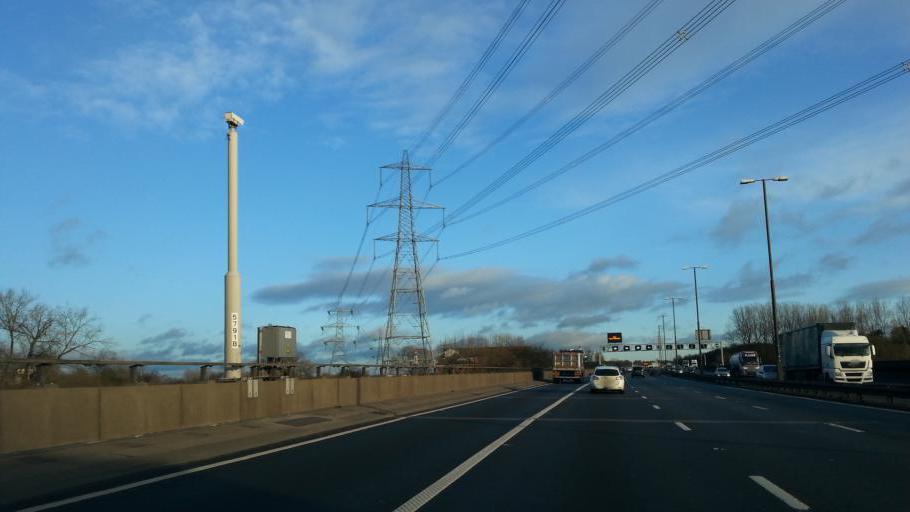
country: GB
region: England
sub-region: City and Borough of Birmingham
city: Sutton Coldfield
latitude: 52.5094
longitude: -1.8027
